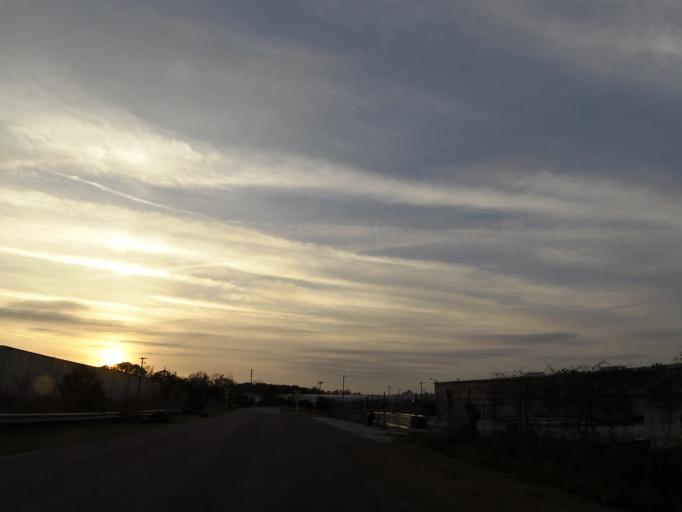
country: US
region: Florida
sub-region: Duval County
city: Jacksonville
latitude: 30.3646
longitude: -81.7121
